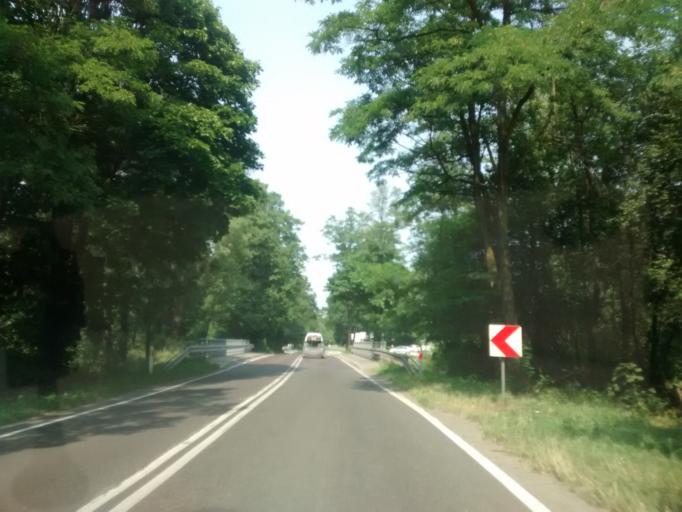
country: PL
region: Lesser Poland Voivodeship
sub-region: Powiat olkuski
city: Klucze
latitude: 50.3553
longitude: 19.5621
